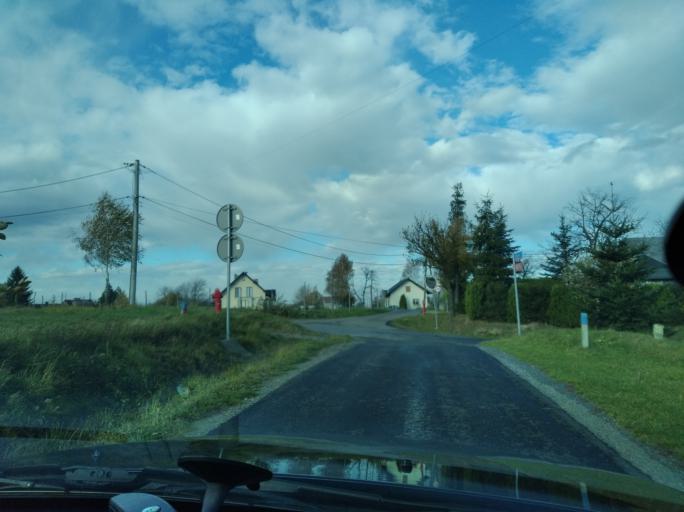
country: PL
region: Subcarpathian Voivodeship
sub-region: Powiat debicki
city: Debica
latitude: 50.0276
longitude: 21.4640
